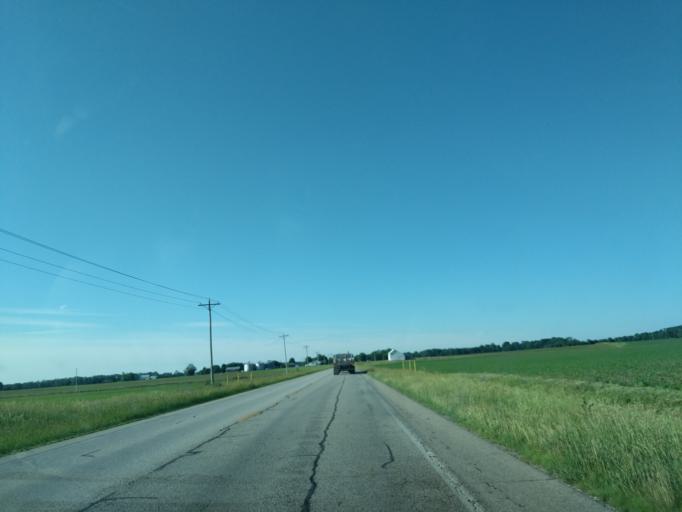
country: US
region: Indiana
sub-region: Shelby County
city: Morristown
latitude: 39.6205
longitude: -85.7673
